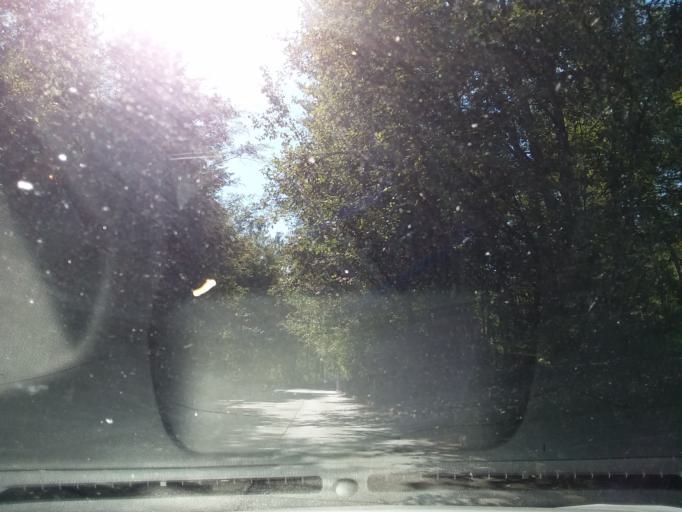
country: US
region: Washington
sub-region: Snohomish County
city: Smokey Point
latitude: 48.1605
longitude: -122.1952
